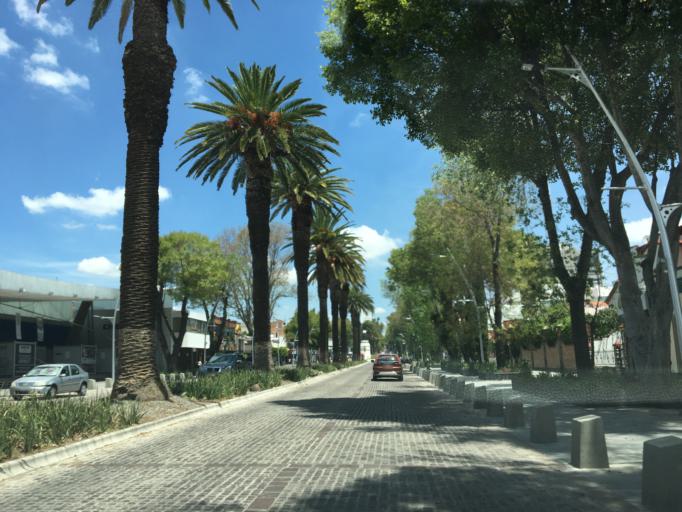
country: MX
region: Puebla
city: Puebla
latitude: 19.0483
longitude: -98.2117
